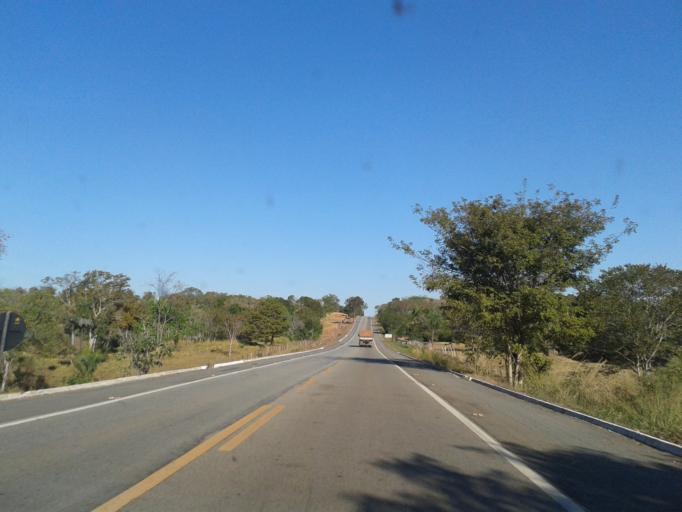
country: BR
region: Goias
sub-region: Mozarlandia
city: Mozarlandia
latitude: -15.2058
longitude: -50.5395
